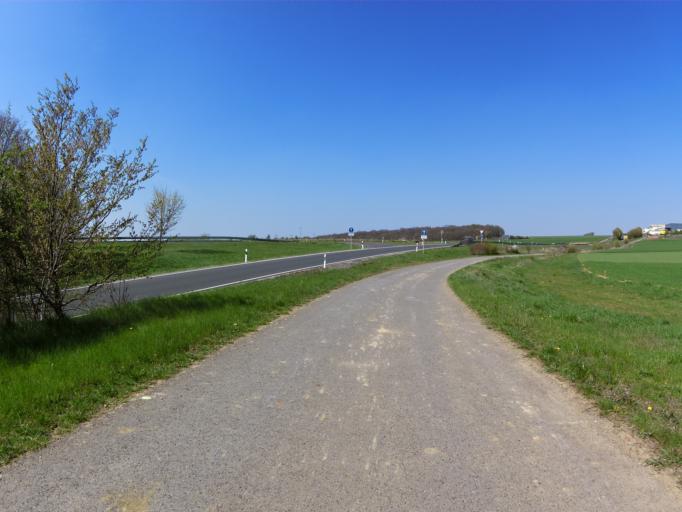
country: DE
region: Bavaria
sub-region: Regierungsbezirk Unterfranken
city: Biebelried
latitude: 49.7736
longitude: 10.0628
